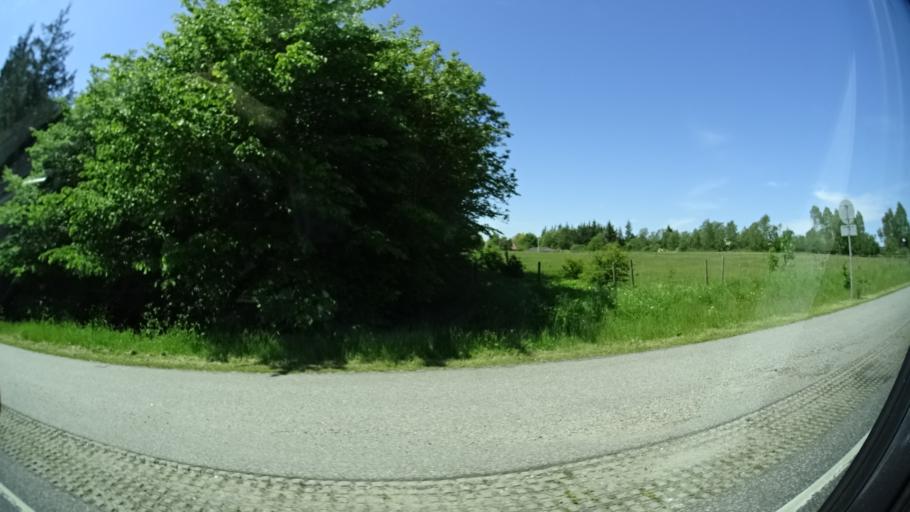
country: DK
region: Central Jutland
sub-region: Arhus Kommune
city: Beder
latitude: 56.0979
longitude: 10.2094
